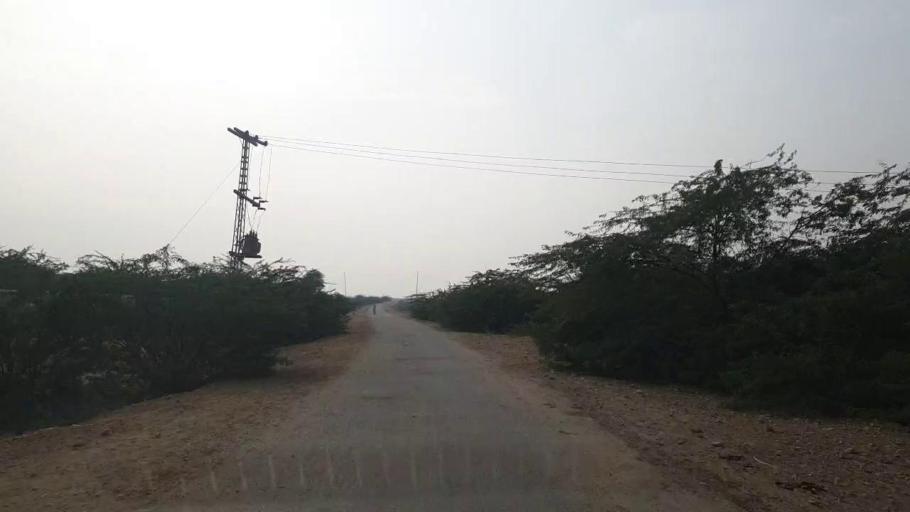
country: PK
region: Sindh
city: Sann
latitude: 26.0561
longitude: 68.1010
